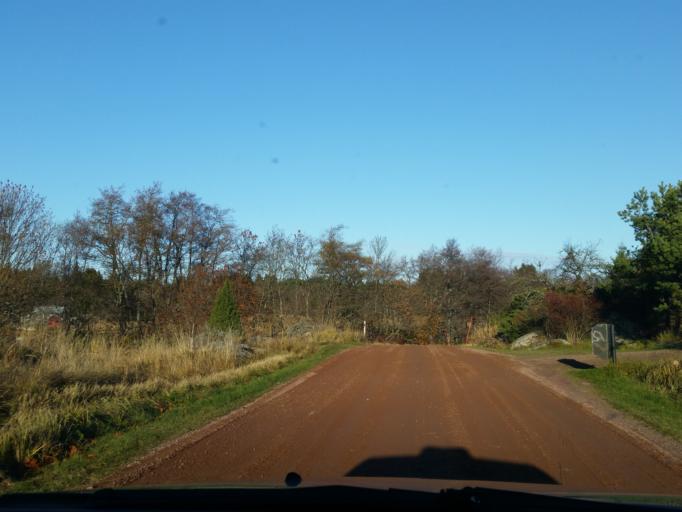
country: AX
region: Alands skaergard
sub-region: Braendoe
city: Braendoe
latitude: 60.4530
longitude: 20.9411
